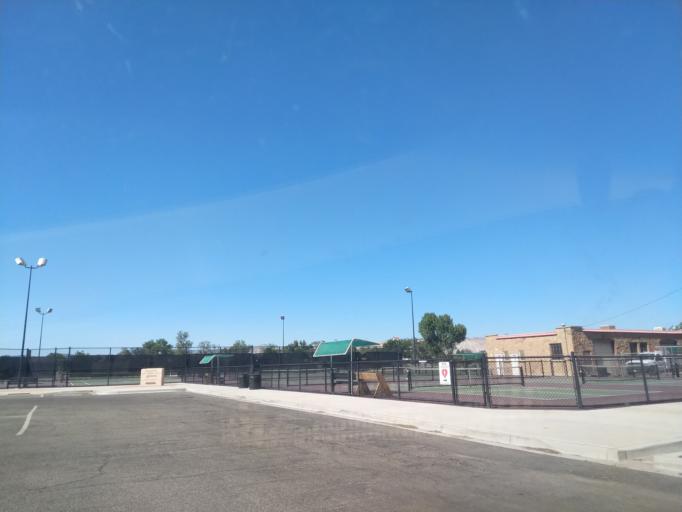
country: US
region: Colorado
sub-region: Mesa County
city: Grand Junction
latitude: 39.0746
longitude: -108.5482
